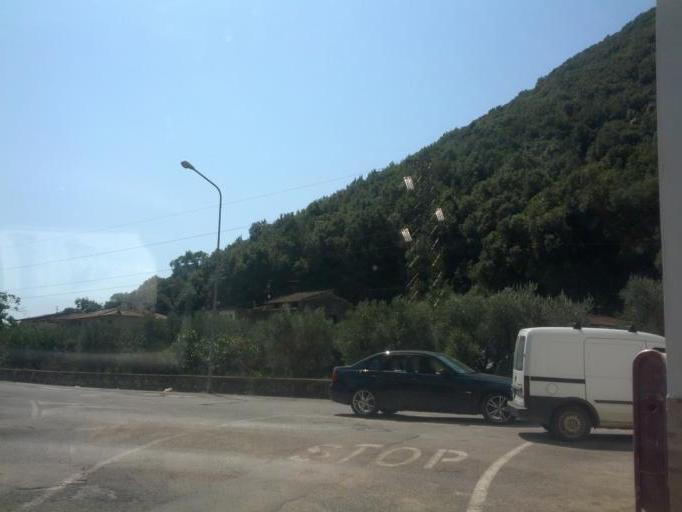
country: IT
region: Latium
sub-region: Provincia di Latina
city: Monte San Biagio
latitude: 41.3678
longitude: 13.3488
